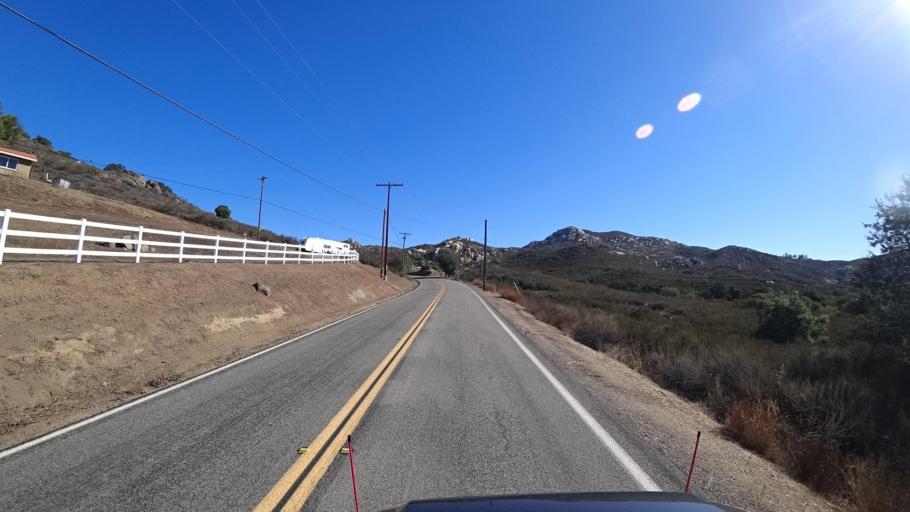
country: US
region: California
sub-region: San Diego County
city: Jamul
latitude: 32.6863
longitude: -116.7508
